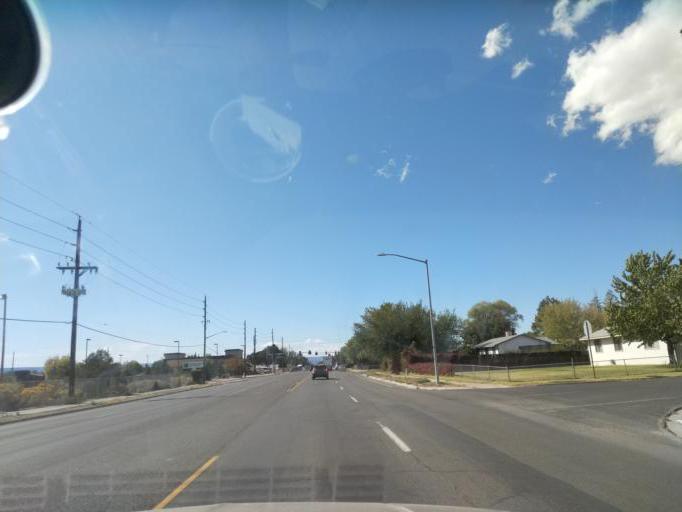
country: US
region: Colorado
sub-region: Mesa County
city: Clifton
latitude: 39.0918
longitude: -108.4572
